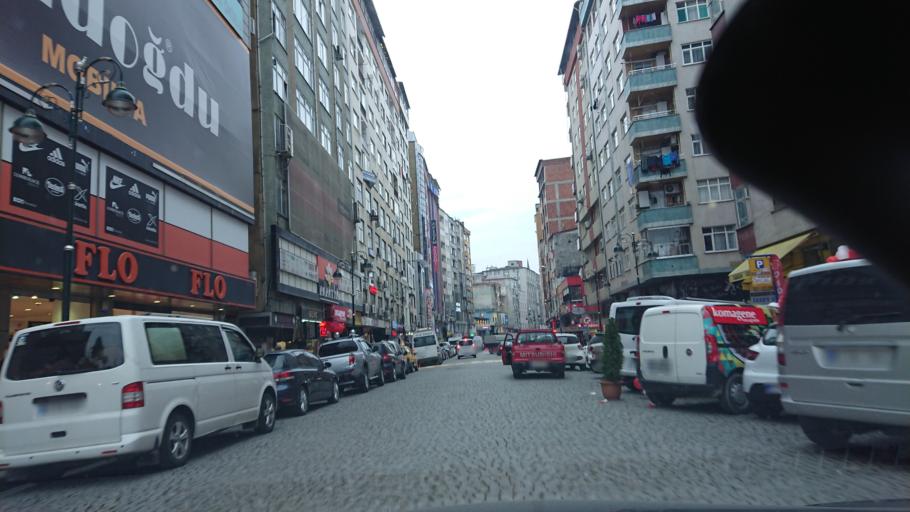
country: TR
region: Rize
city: Rize
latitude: 41.0249
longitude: 40.5243
